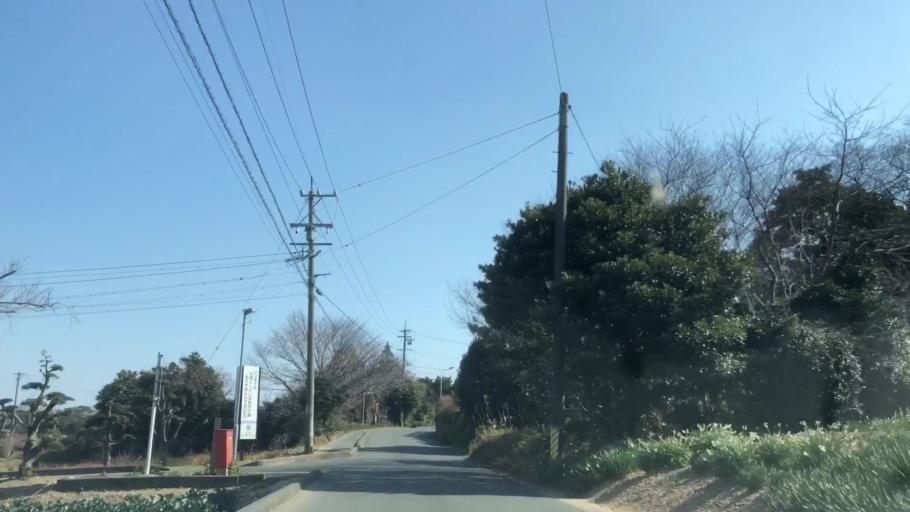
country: JP
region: Aichi
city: Tahara
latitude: 34.6676
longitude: 137.2553
